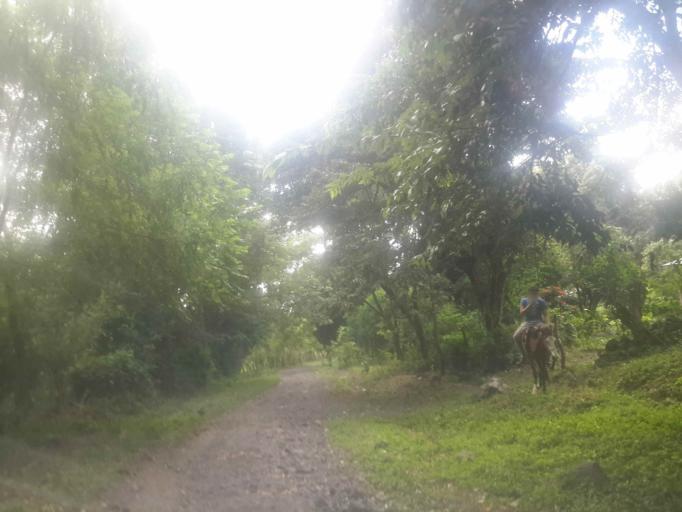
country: NI
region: Rivas
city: Altagracia
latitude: 11.5100
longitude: -85.6047
